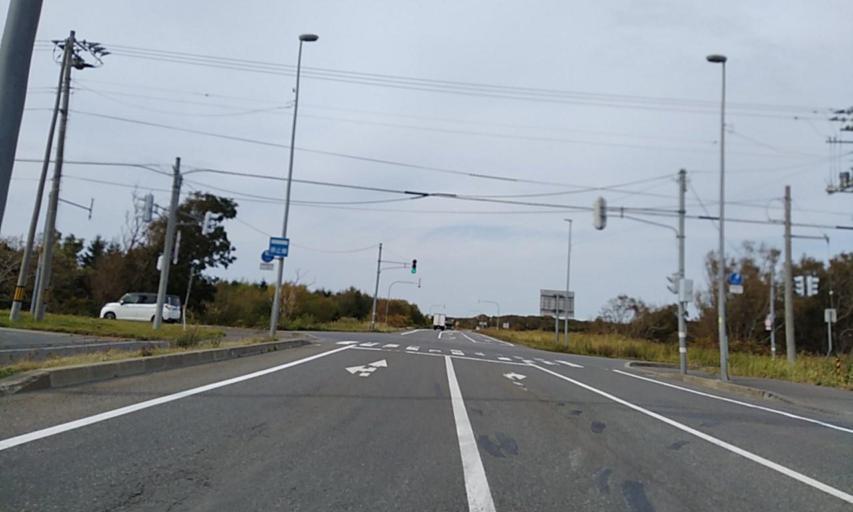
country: JP
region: Hokkaido
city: Makubetsu
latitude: 44.8921
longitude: 141.7467
